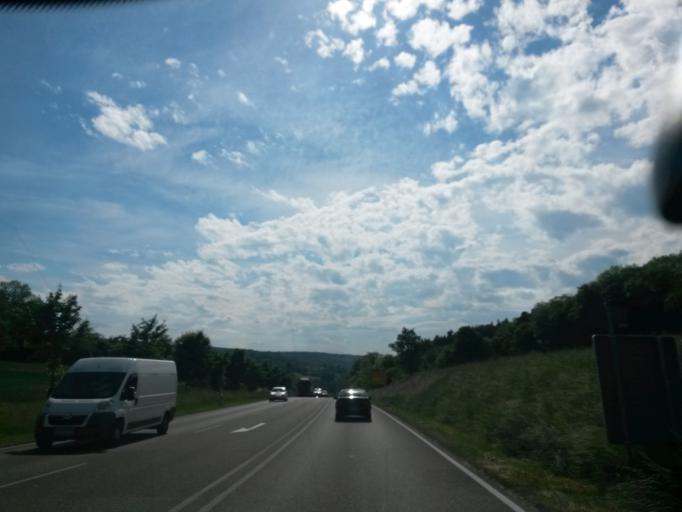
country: DE
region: Baden-Wuerttemberg
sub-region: Regierungsbezirk Stuttgart
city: Weil der Stadt
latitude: 48.7491
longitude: 8.8856
